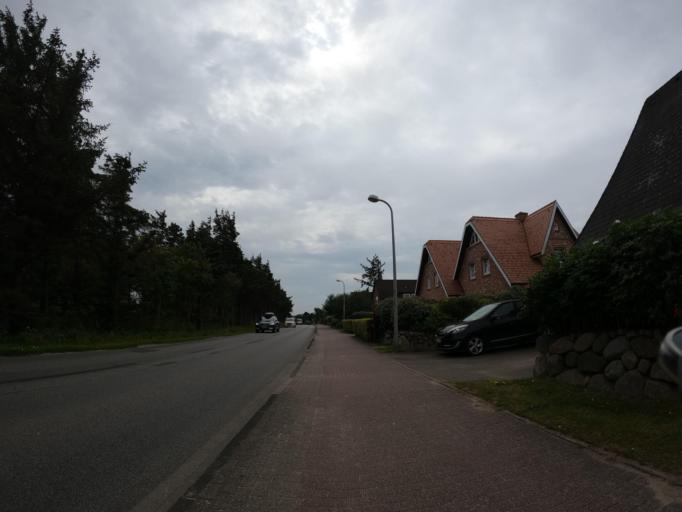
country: DE
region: Schleswig-Holstein
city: Westerland
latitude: 54.9219
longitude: 8.3108
